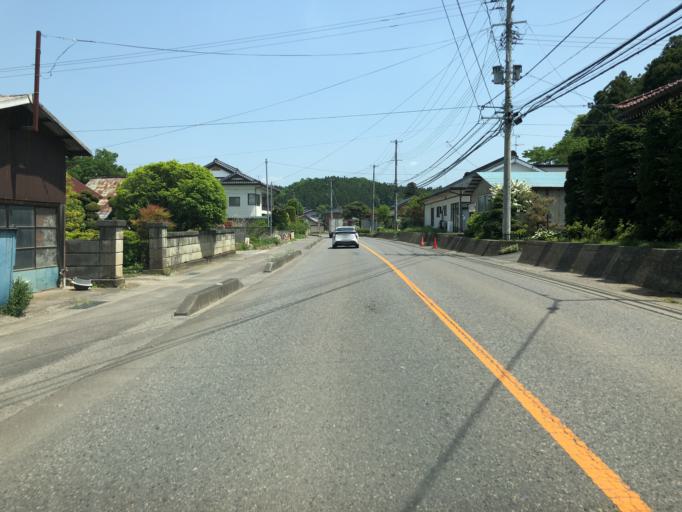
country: JP
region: Fukushima
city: Ishikawa
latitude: 37.1422
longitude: 140.4062
